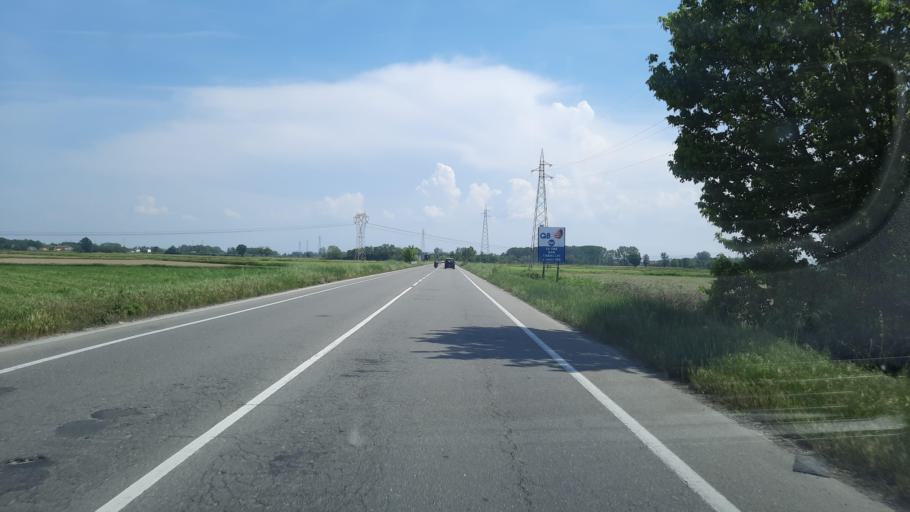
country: IT
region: Lombardy
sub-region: Provincia di Pavia
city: Gropello Cairoli
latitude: 45.1737
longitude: 8.9737
